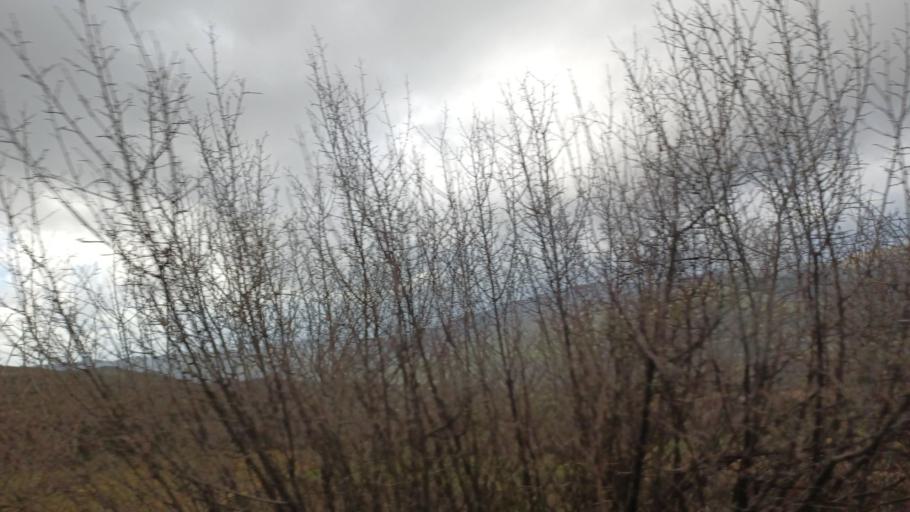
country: CY
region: Limassol
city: Pachna
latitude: 34.8376
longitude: 32.7435
